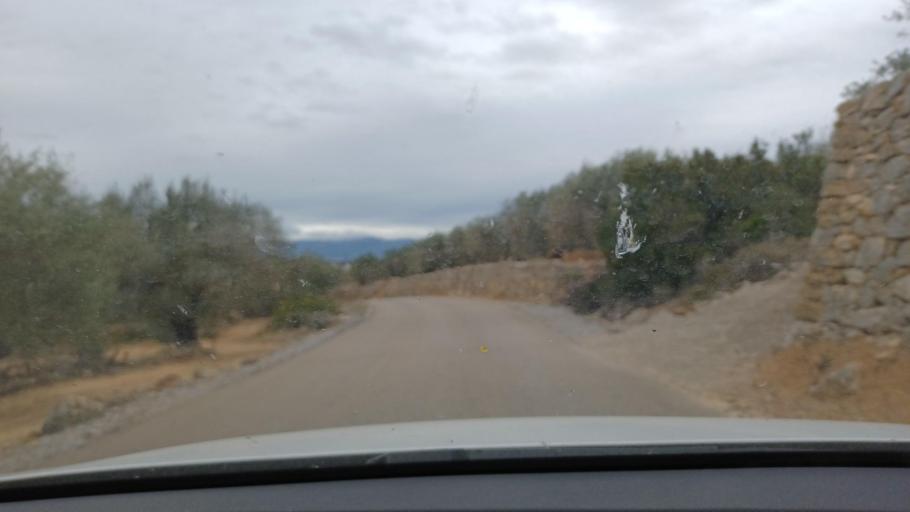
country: ES
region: Valencia
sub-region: Provincia de Castello
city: Traiguera
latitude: 40.5094
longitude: 0.2948
